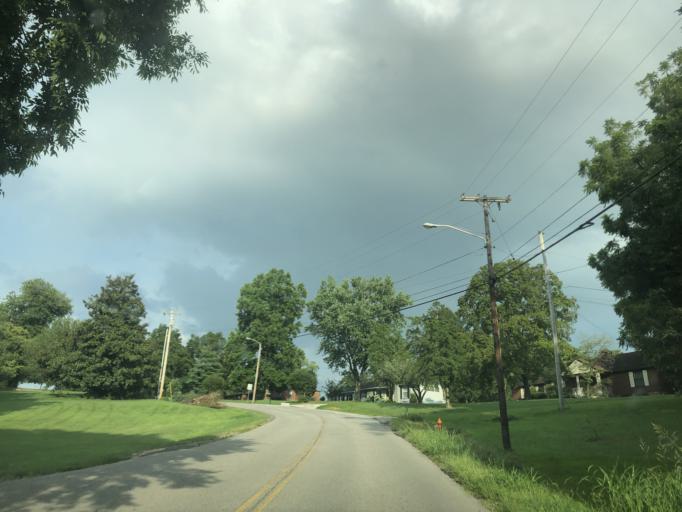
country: US
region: Tennessee
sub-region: Davidson County
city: Lakewood
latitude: 36.1545
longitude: -86.6797
